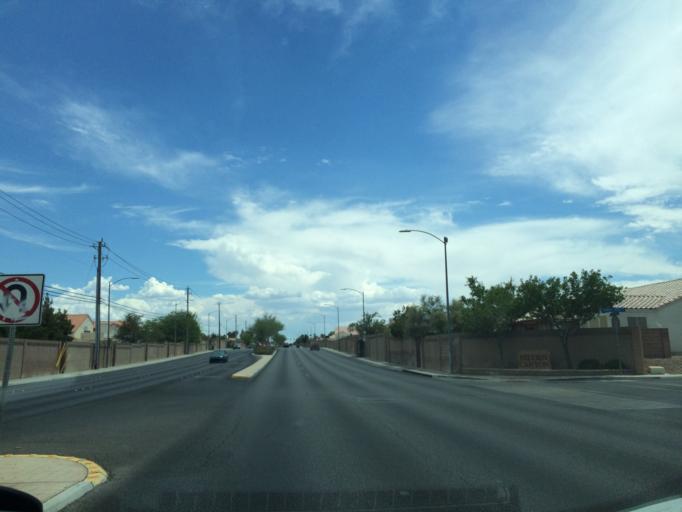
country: US
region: Nevada
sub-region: Clark County
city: North Las Vegas
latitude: 36.2301
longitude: -115.1620
